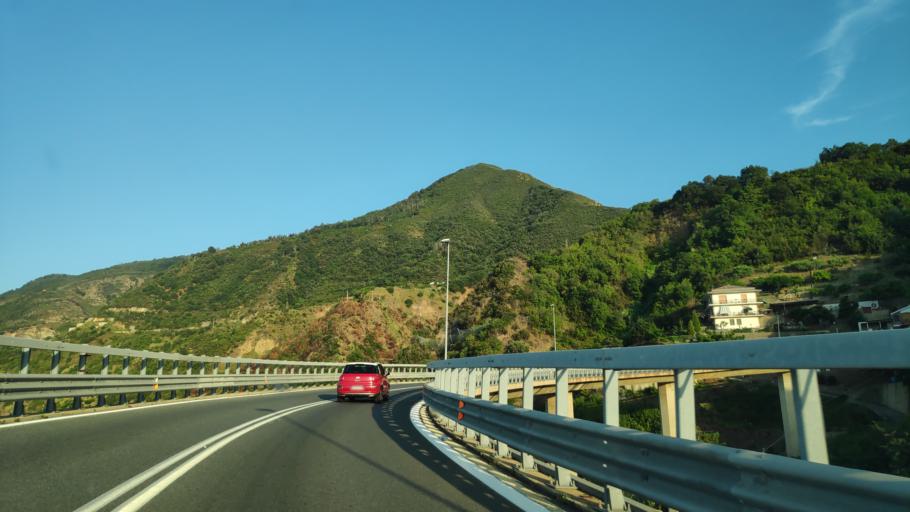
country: IT
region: Calabria
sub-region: Provincia di Reggio Calabria
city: Scilla
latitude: 38.2528
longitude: 15.7277
